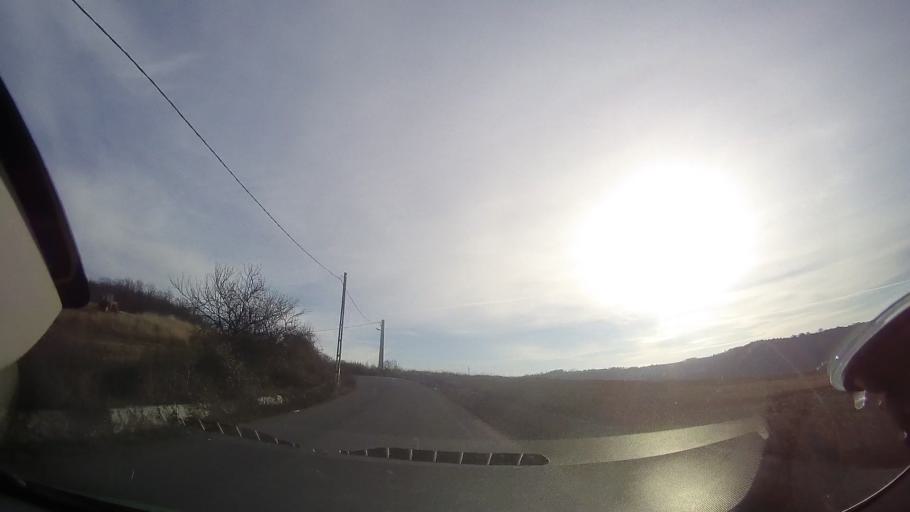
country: RO
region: Bihor
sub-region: Comuna Sarbi
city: Burzuc
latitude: 47.1373
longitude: 22.1836
